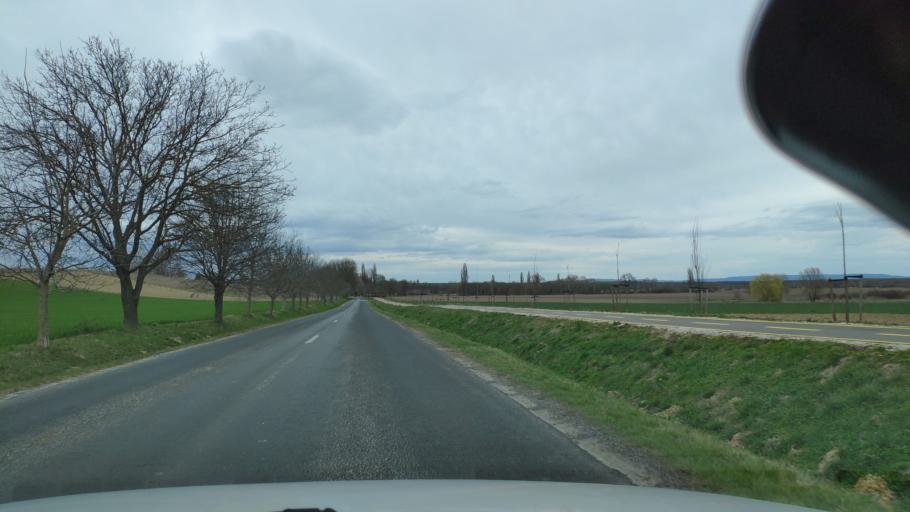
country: HU
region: Zala
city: Zalakomar
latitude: 46.5716
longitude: 17.1239
